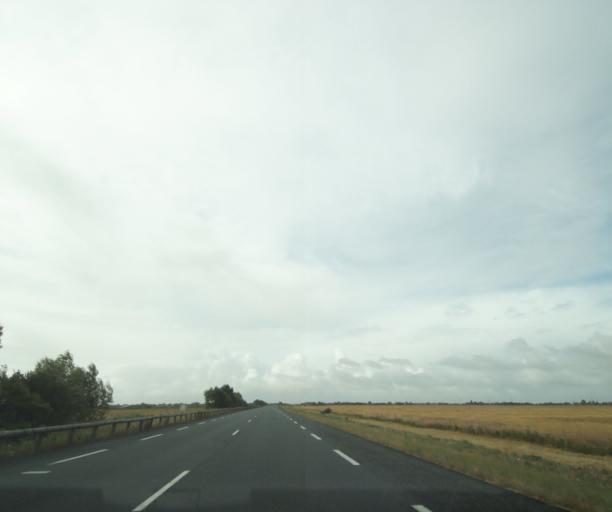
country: FR
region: Pays de la Loire
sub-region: Departement de la Vendee
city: Champagne-les-Marais
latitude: 46.3951
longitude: -1.0951
